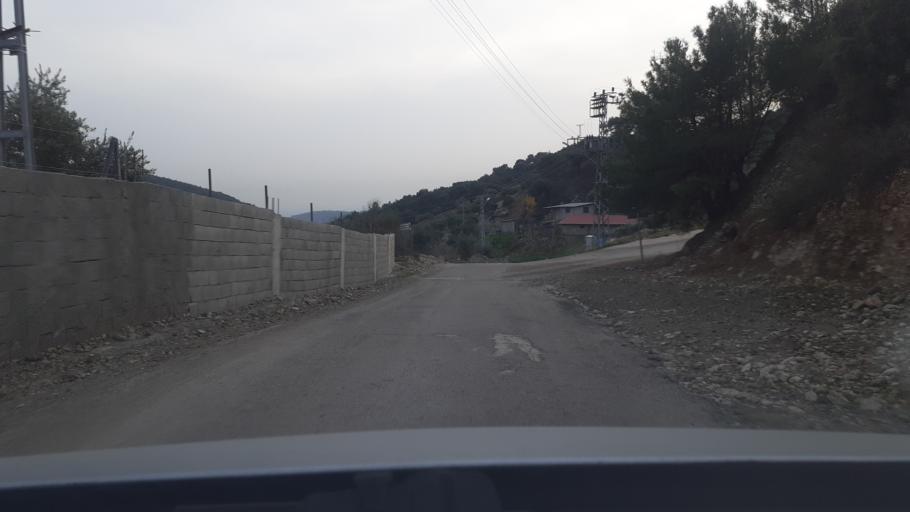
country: TR
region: Hatay
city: Kirikhan
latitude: 36.5287
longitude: 36.3168
